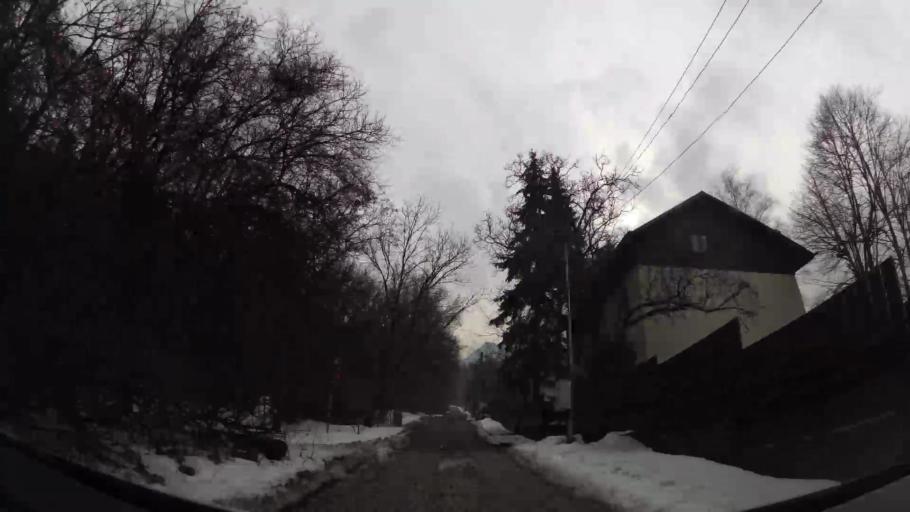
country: BG
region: Sofia-Capital
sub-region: Stolichna Obshtina
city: Sofia
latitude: 42.6549
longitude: 23.2387
